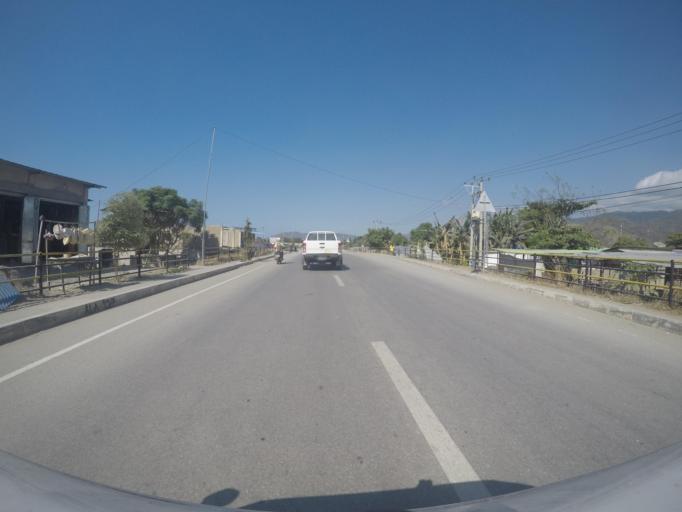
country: TL
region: Dili
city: Dili
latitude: -8.5618
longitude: 125.5317
